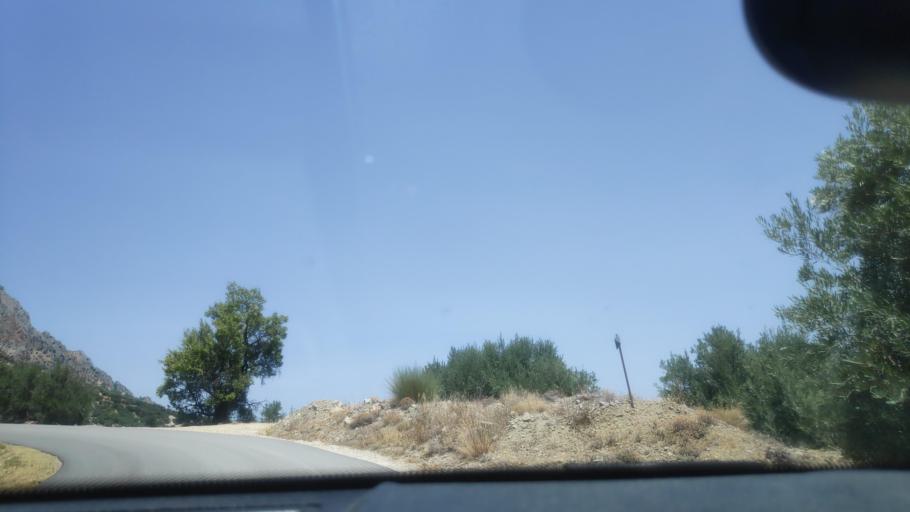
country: ES
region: Andalusia
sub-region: Provincia de Jaen
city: Torres
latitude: 37.7872
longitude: -3.4591
